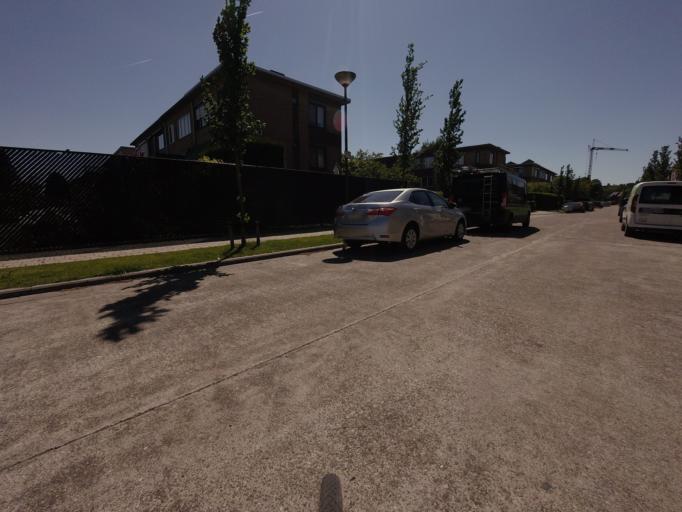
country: BE
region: Flanders
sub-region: Provincie Antwerpen
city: Hove
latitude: 51.1734
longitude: 4.4773
